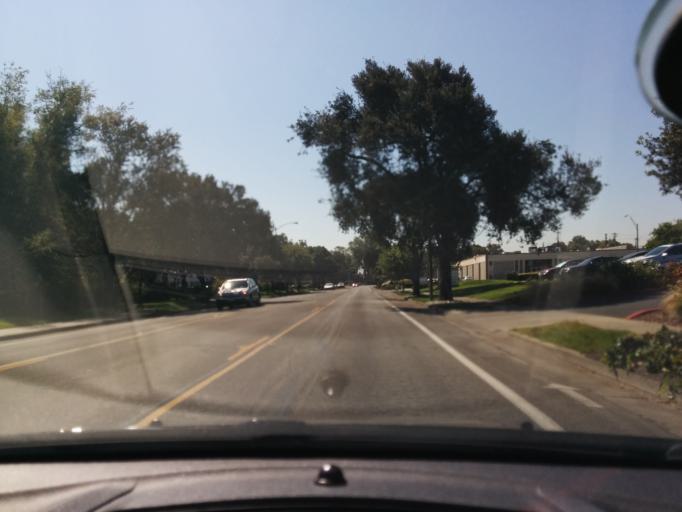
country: US
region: California
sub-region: Santa Clara County
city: Sunnyvale
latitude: 37.3832
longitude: -122.0073
